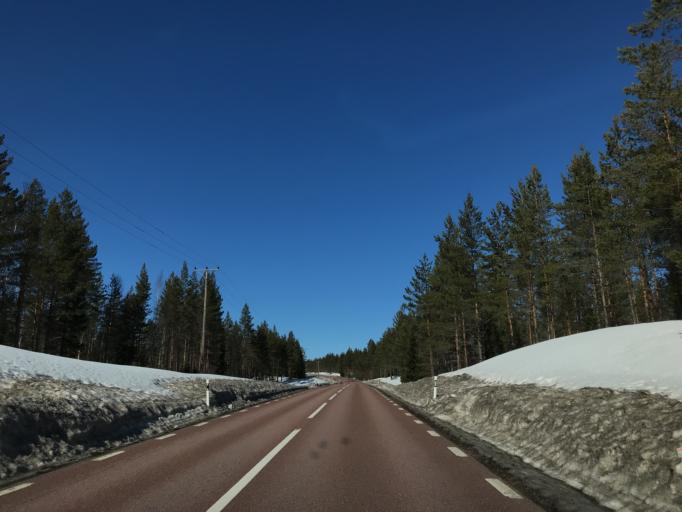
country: SE
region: Vaermland
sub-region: Filipstads Kommun
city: Lesjofors
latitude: 60.1741
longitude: 14.1982
